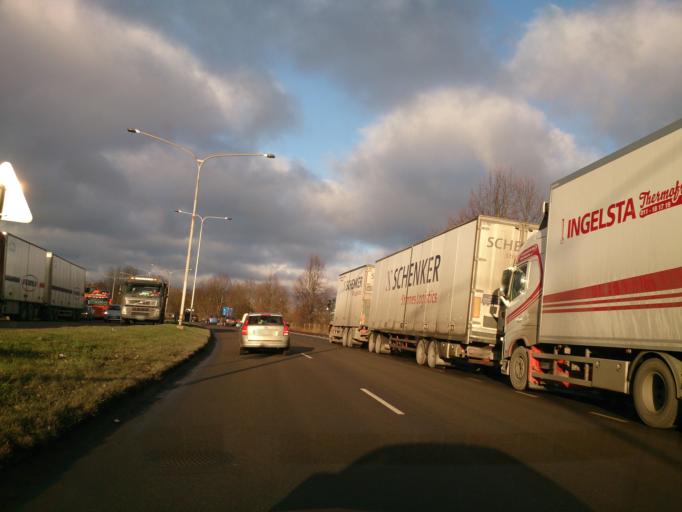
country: SE
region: OEstergoetland
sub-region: Norrkopings Kommun
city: Norrkoping
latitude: 58.6042
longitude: 16.1664
